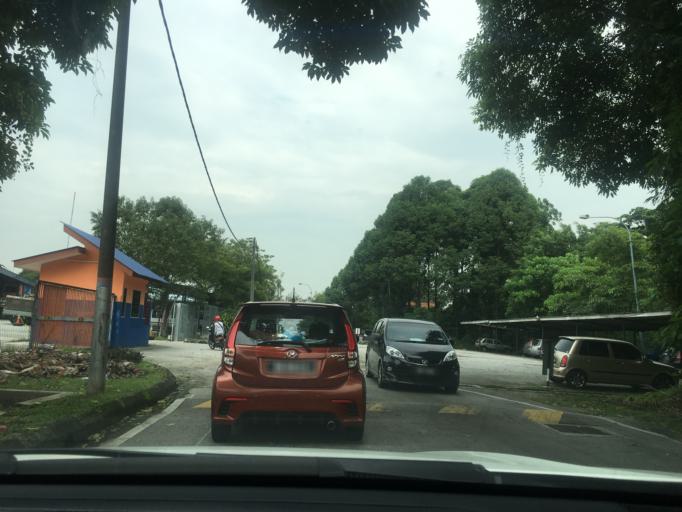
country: MY
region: Selangor
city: Klang
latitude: 3.0475
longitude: 101.4406
